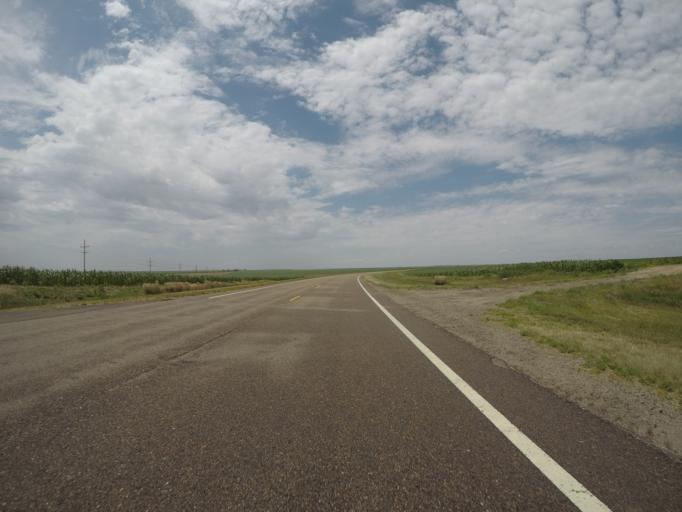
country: US
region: Kansas
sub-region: Thomas County
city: Colby
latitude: 39.3804
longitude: -100.8144
